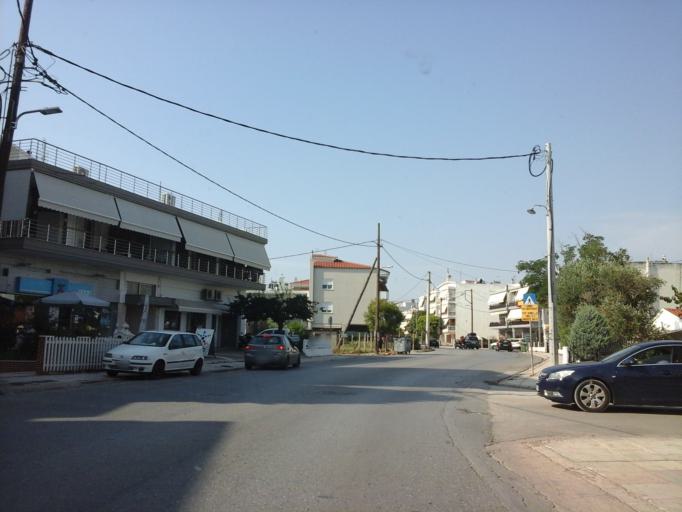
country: GR
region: East Macedonia and Thrace
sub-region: Nomos Evrou
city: Alexandroupoli
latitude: 40.8570
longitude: 25.8692
